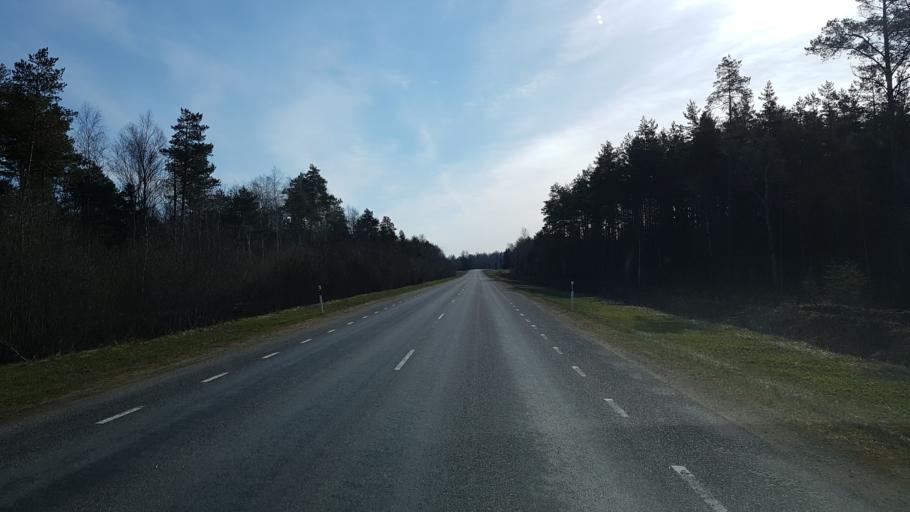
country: EE
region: Ida-Virumaa
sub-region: Aseri vald
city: Aseri
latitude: 59.3550
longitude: 26.7141
